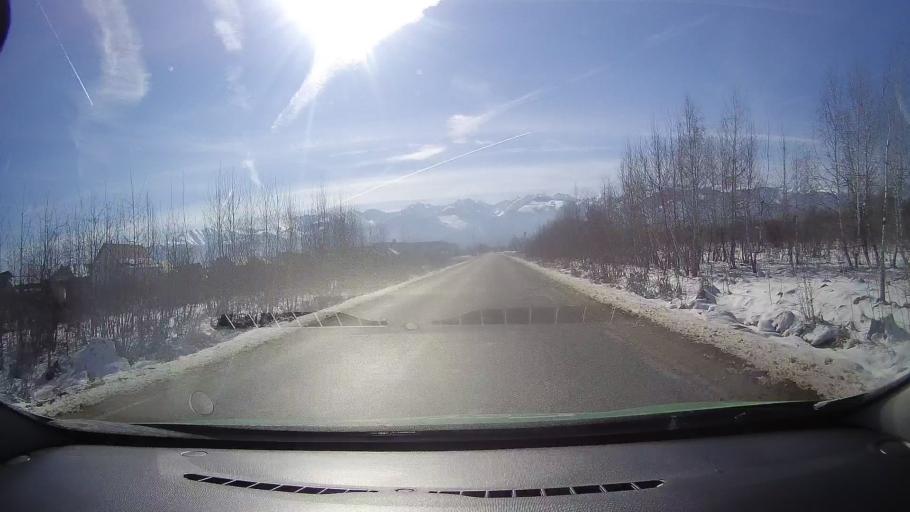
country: RO
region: Brasov
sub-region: Oras Victoria
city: Victoria
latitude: 45.7370
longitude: 24.6949
